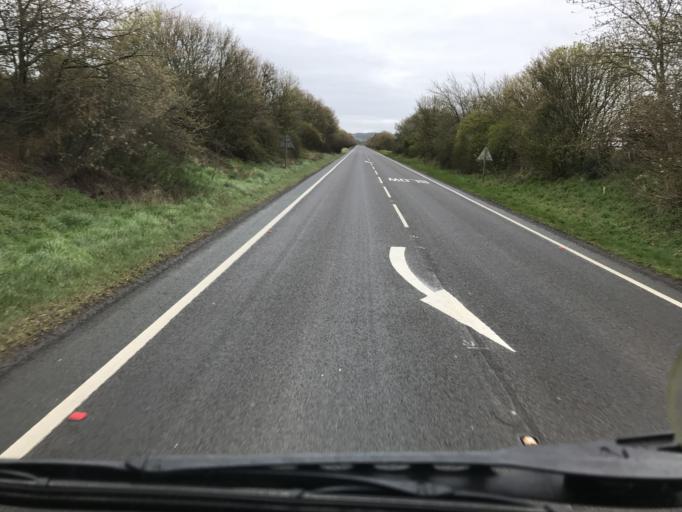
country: GB
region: England
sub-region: Cheshire West and Chester
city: Tattenhall
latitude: 53.1168
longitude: -2.7975
